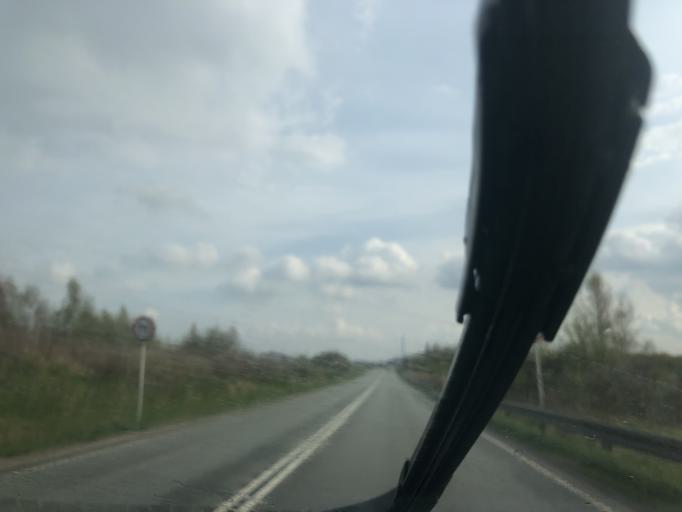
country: DK
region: Zealand
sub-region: Roskilde Kommune
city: Roskilde
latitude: 55.6634
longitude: 12.1172
